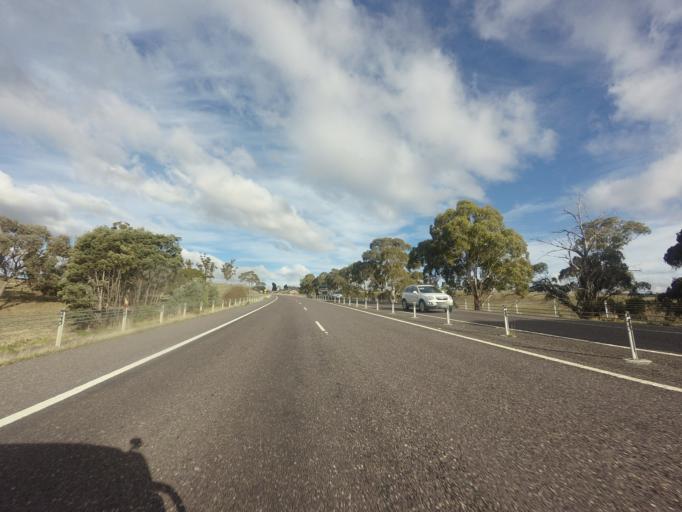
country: AU
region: Tasmania
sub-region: Brighton
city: Bridgewater
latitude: -42.5675
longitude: 147.2096
